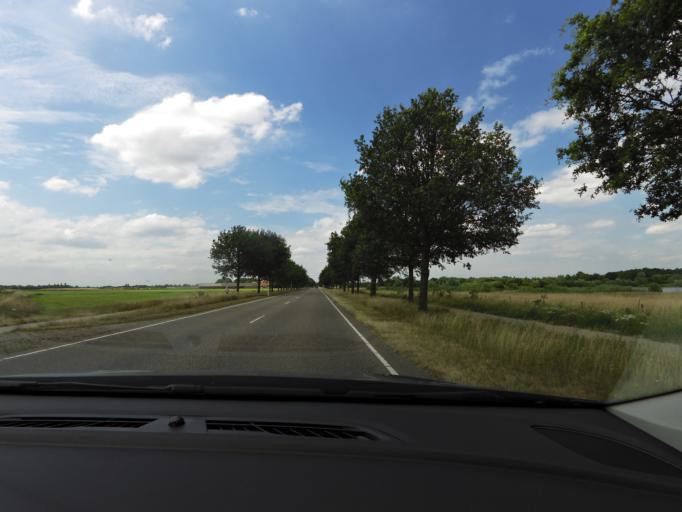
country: NL
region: North Brabant
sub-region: Gemeente Baarle-Nassau
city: Baarle-Nassau
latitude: 51.4837
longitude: 4.8857
